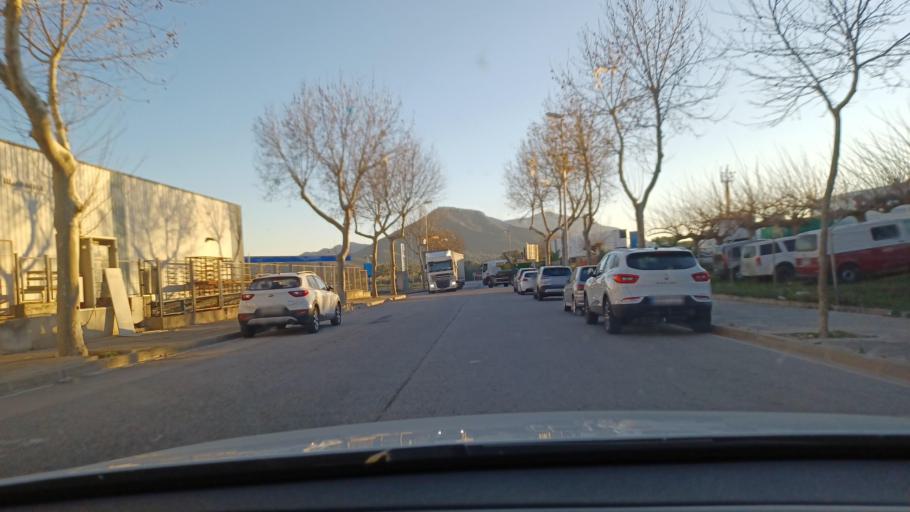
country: ES
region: Catalonia
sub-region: Provincia de Tarragona
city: Amposta
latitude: 40.7033
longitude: 0.5584
